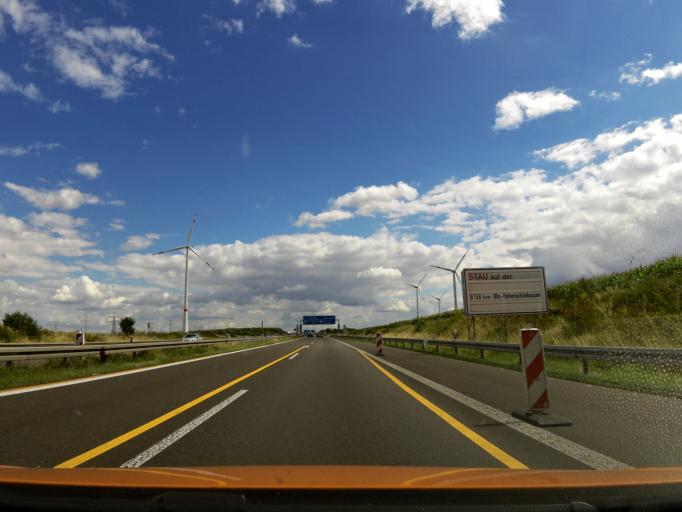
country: DE
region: Berlin
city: Buch
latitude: 52.6164
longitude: 13.5228
